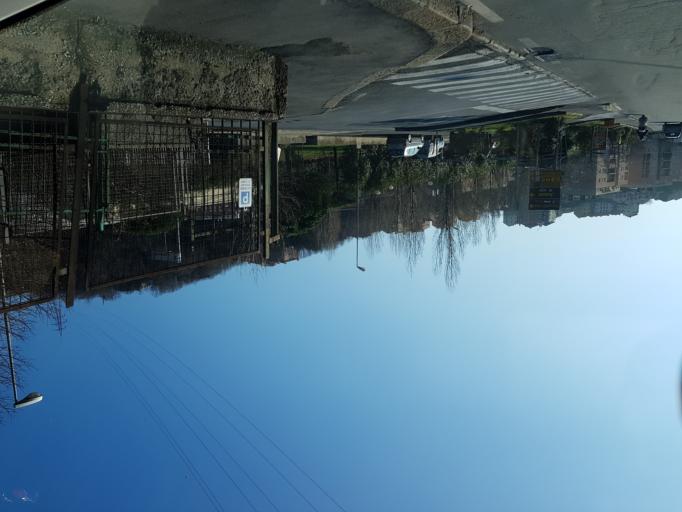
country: IT
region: Liguria
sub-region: Provincia di Genova
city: Santa Marta
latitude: 44.4770
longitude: 8.8994
